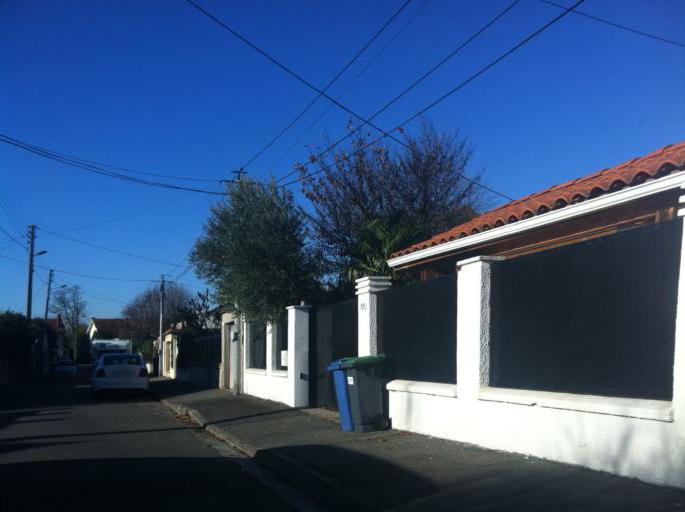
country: FR
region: Midi-Pyrenees
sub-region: Departement de la Haute-Garonne
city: Toulouse
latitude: 43.5816
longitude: 1.4683
